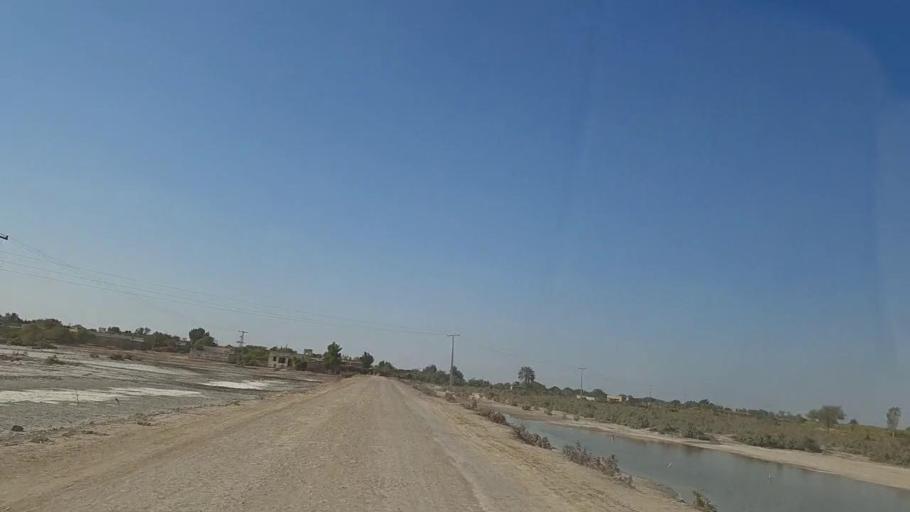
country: PK
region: Sindh
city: Digri
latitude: 25.1755
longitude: 69.0139
